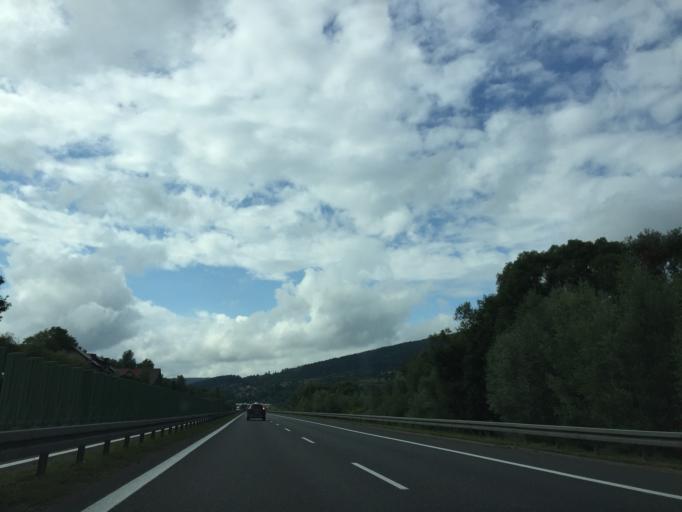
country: PL
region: Lesser Poland Voivodeship
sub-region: Powiat myslenicki
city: Pcim
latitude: 49.7773
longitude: 19.9565
